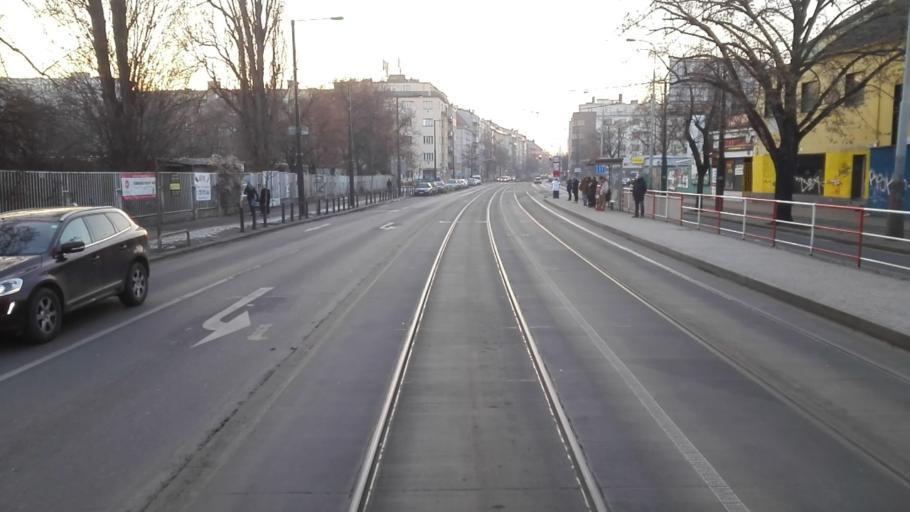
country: CZ
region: Praha
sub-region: Praha 8
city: Karlin
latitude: 50.0663
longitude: 14.4548
